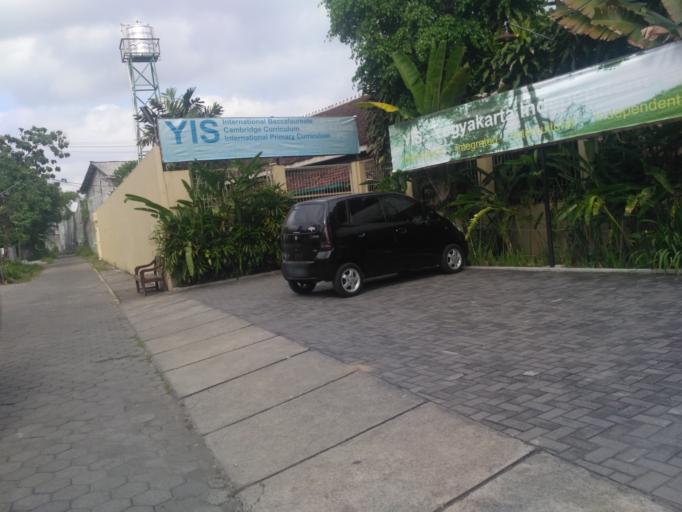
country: ID
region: Daerah Istimewa Yogyakarta
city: Melati
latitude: -7.7557
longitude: 110.3643
